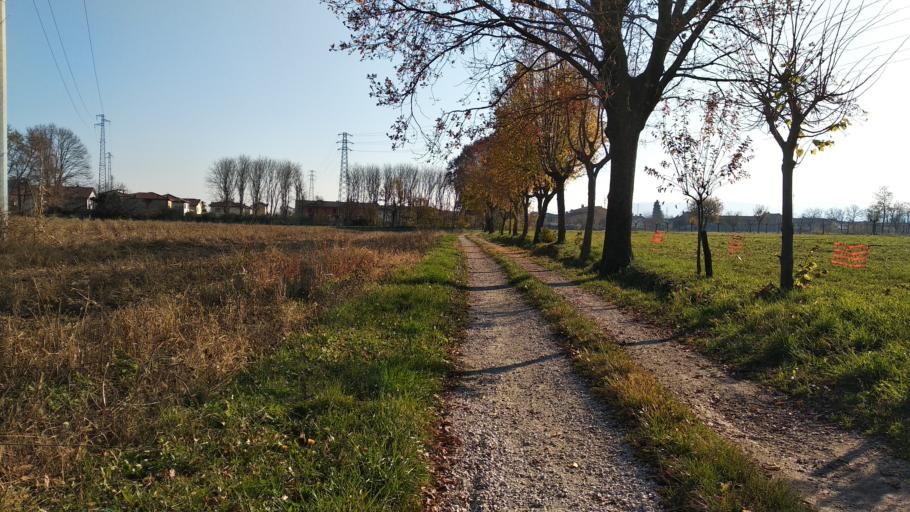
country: IT
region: Veneto
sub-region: Provincia di Vicenza
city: Schio
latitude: 45.7021
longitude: 11.3726
